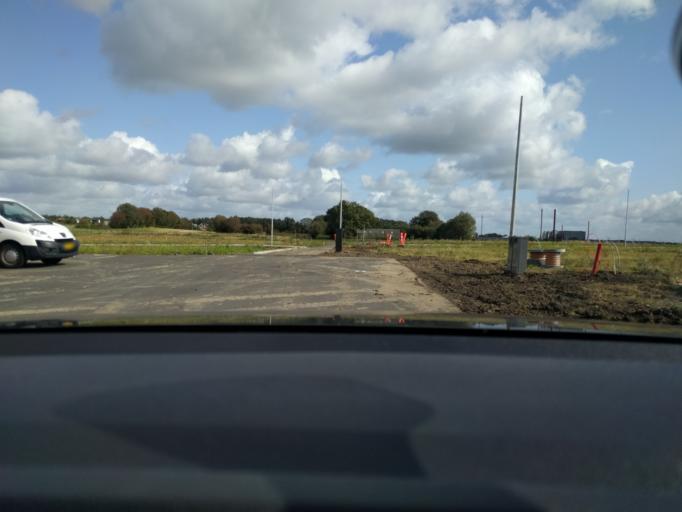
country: DK
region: Central Jutland
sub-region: Favrskov Kommune
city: Hammel
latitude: 56.2416
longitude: 9.8475
